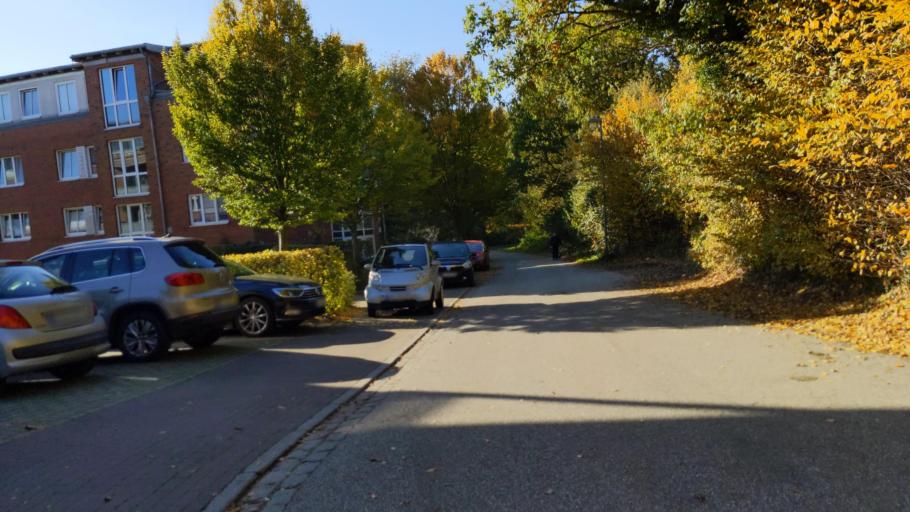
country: DE
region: Mecklenburg-Vorpommern
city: Selmsdorf
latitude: 53.9238
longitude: 10.8277
